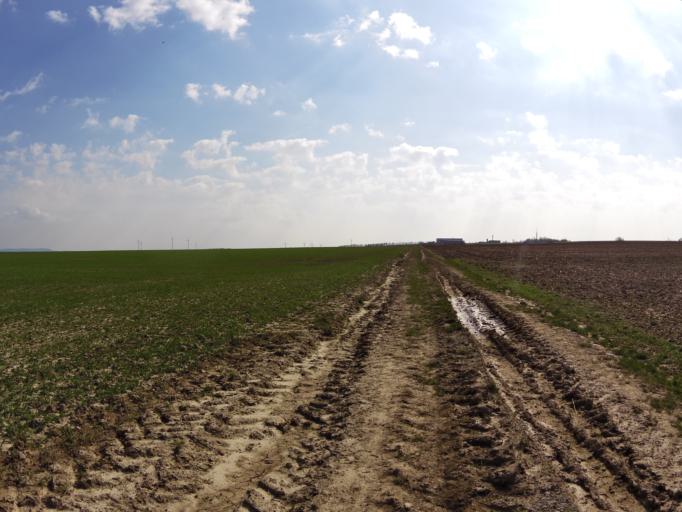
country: DE
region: Bavaria
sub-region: Regierungsbezirk Unterfranken
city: Rottendorf
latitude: 49.7960
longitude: 10.0653
